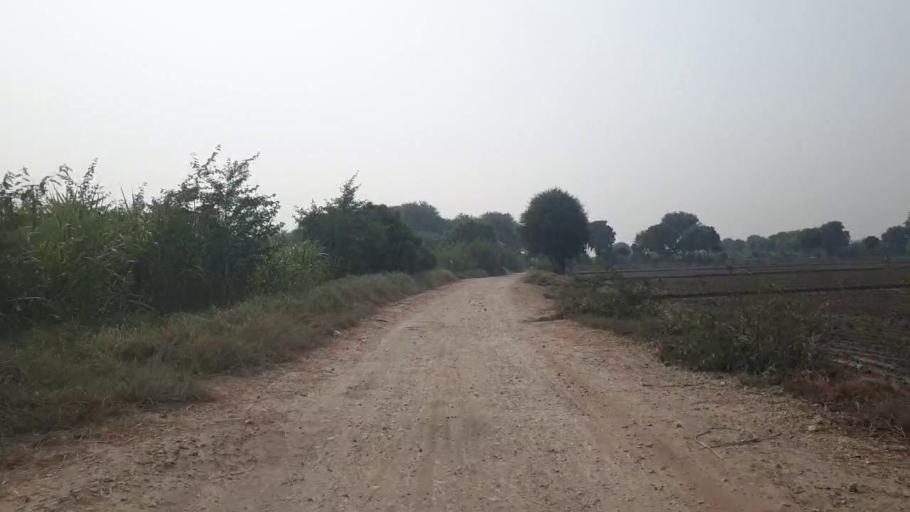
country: PK
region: Sindh
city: Tando Muhammad Khan
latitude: 25.2367
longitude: 68.5703
